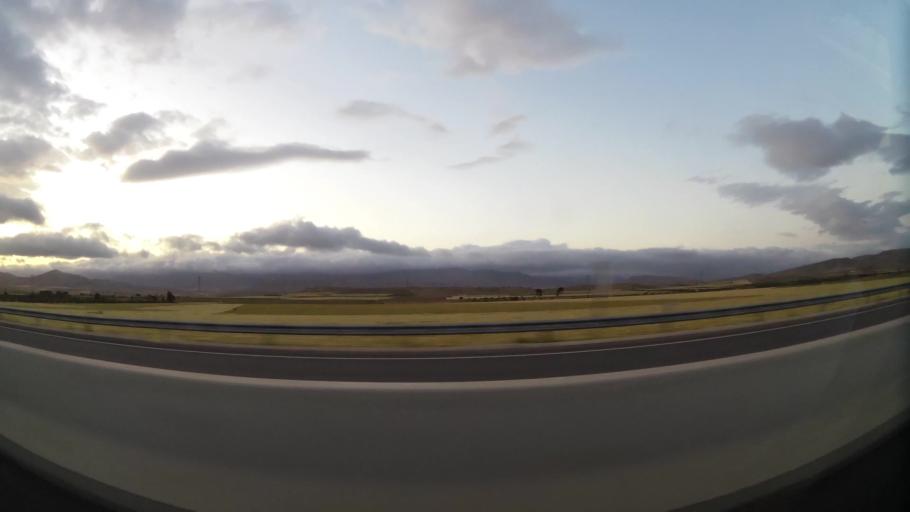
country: MA
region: Oriental
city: El Aioun
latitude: 34.6262
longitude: -2.5195
